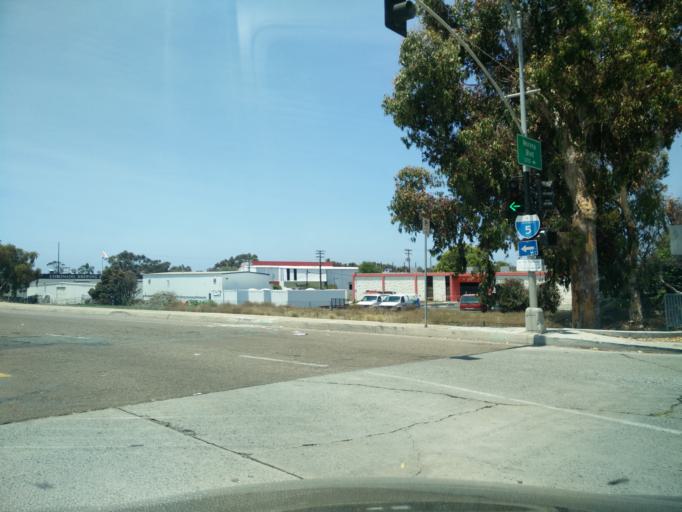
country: US
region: California
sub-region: San Diego County
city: San Diego
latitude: 32.7727
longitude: -117.2028
